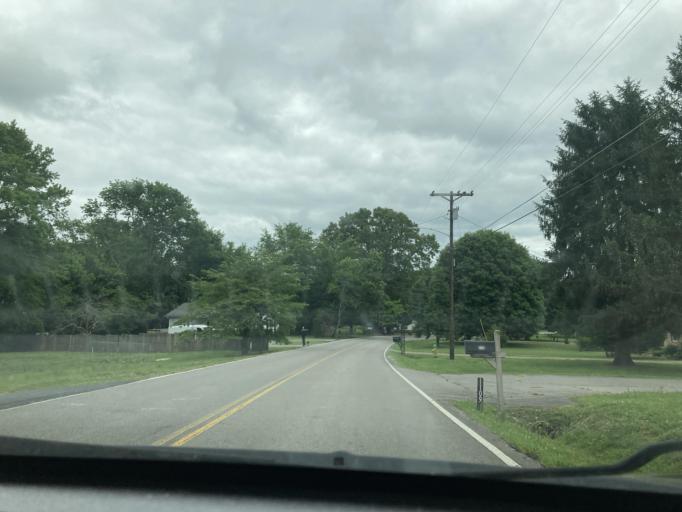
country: US
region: Tennessee
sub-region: Dickson County
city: Dickson
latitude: 36.0939
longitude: -87.3804
